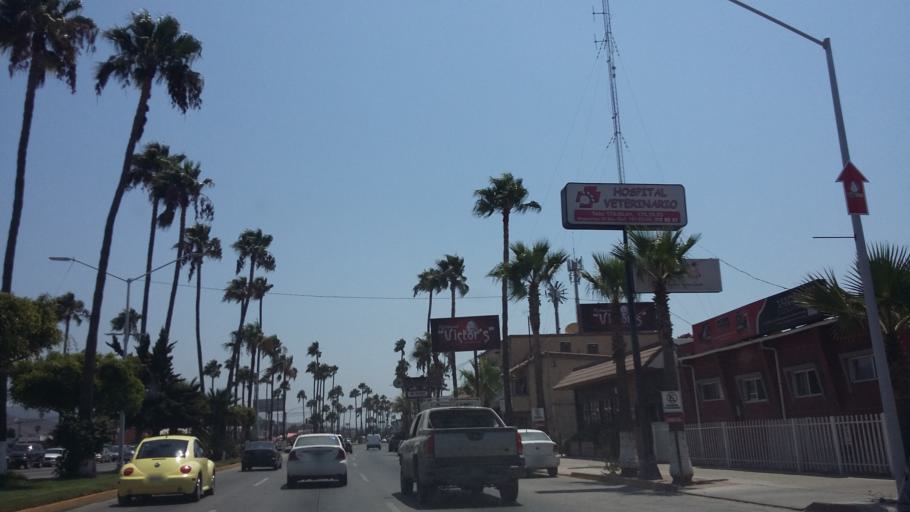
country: MX
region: Baja California
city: Ensenada
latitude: 31.8554
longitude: -116.6178
